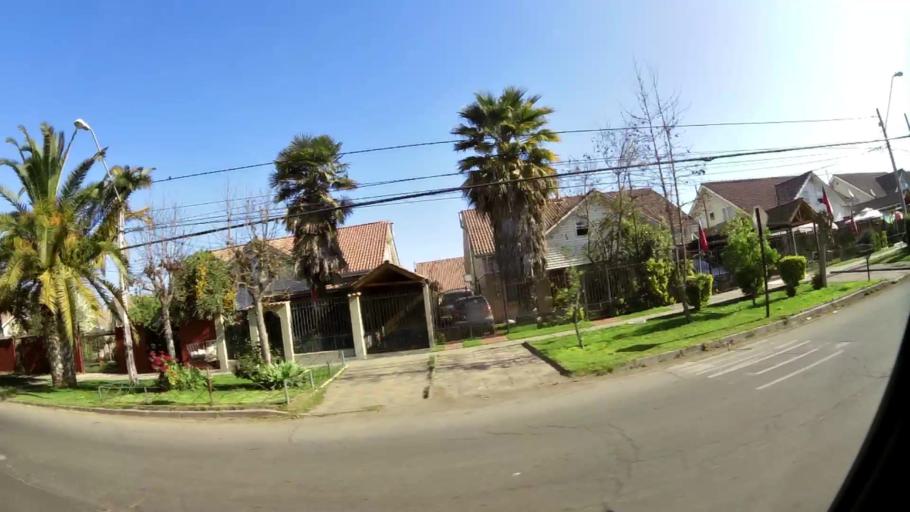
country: CL
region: Santiago Metropolitan
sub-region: Provincia de Santiago
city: Lo Prado
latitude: -33.4889
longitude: -70.7760
